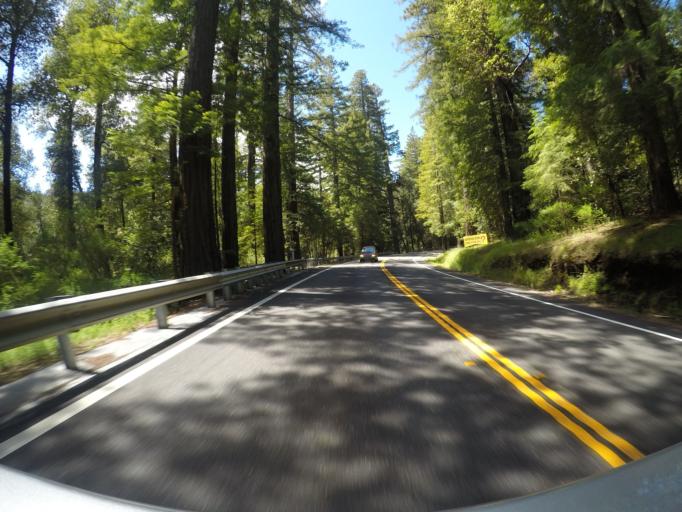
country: US
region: California
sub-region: Humboldt County
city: Redway
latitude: 39.9167
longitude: -123.7668
